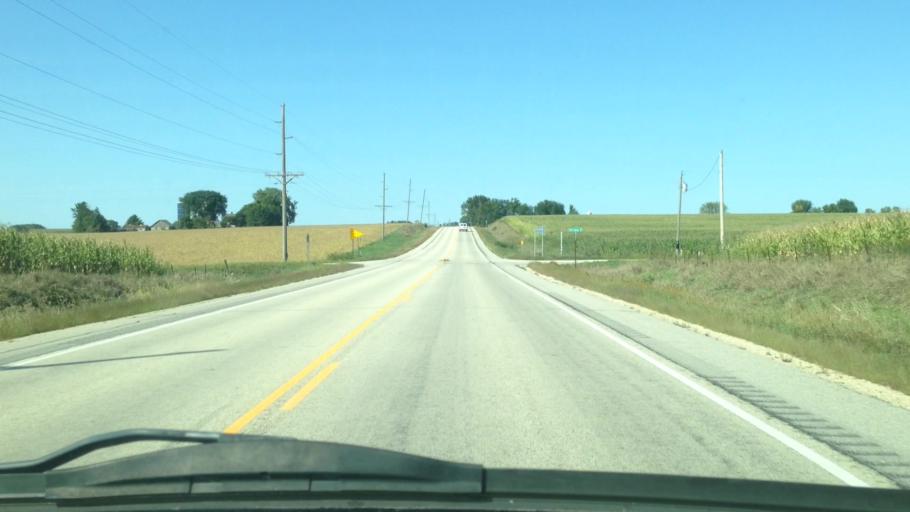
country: US
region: Minnesota
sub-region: Fillmore County
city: Rushford
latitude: 43.9036
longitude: -91.7401
